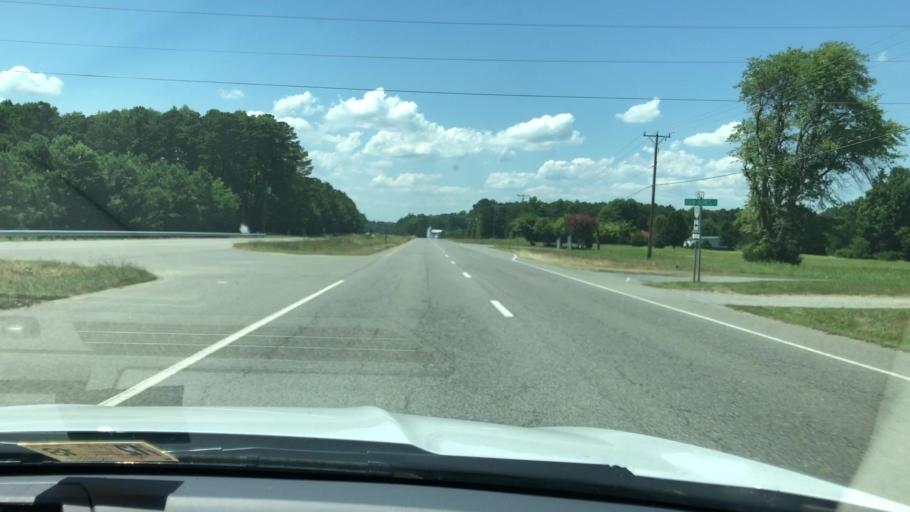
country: US
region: Virginia
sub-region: Middlesex County
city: Saluda
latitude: 37.6044
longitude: -76.5343
